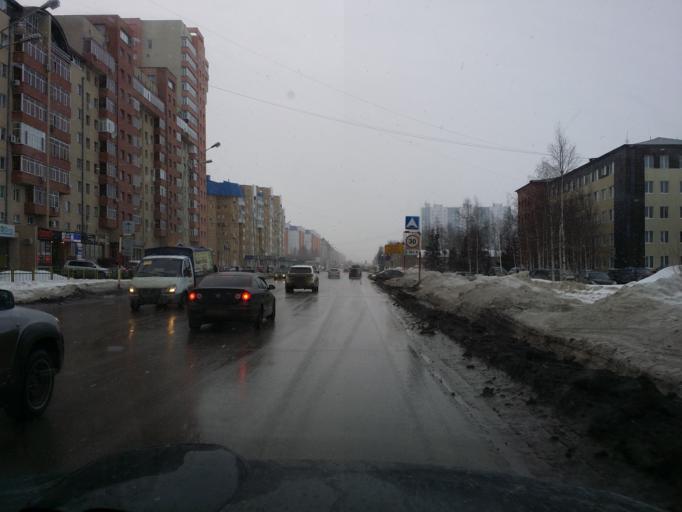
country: RU
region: Khanty-Mansiyskiy Avtonomnyy Okrug
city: Nizhnevartovsk
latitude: 60.9307
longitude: 76.5709
